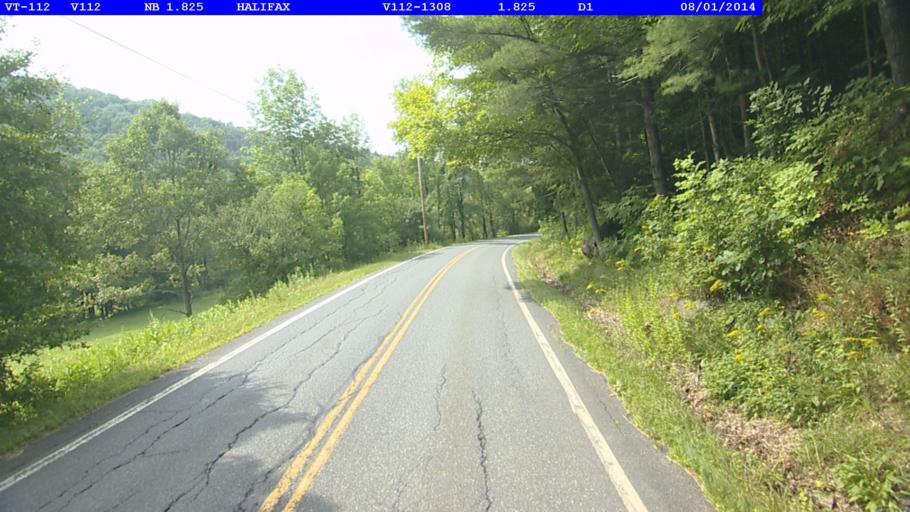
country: US
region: Massachusetts
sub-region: Franklin County
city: Colrain
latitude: 42.7476
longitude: -72.7498
